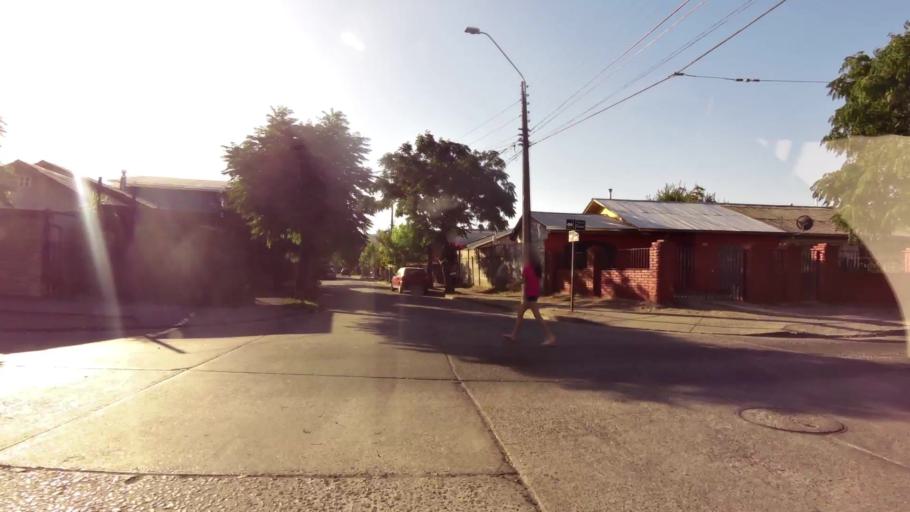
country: CL
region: Maule
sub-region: Provincia de Talca
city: Talca
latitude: -35.4370
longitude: -71.6902
